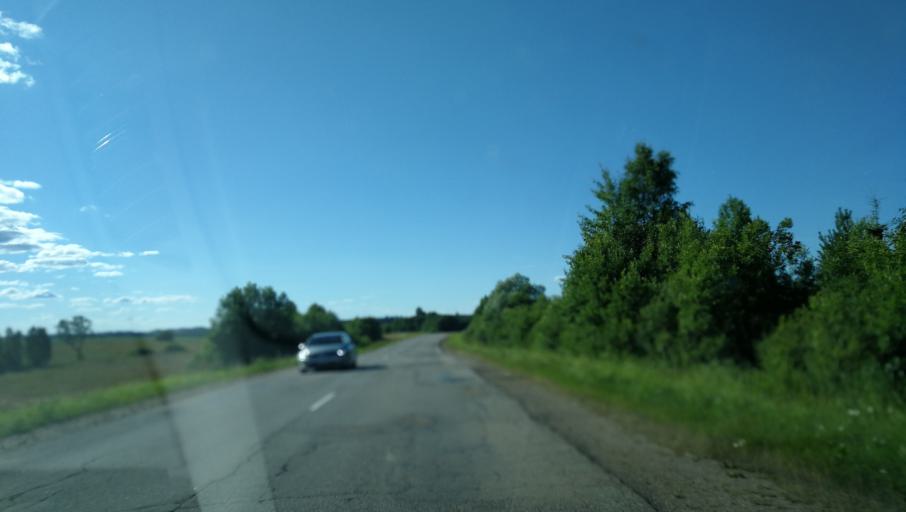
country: LV
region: Jaunpiebalga
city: Jaunpiebalga
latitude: 56.9852
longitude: 26.0216
